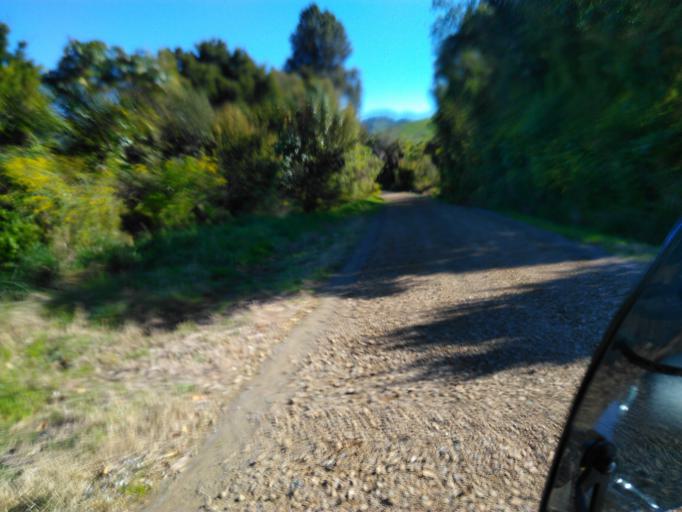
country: NZ
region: Gisborne
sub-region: Gisborne District
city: Gisborne
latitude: -38.3812
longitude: 177.6184
